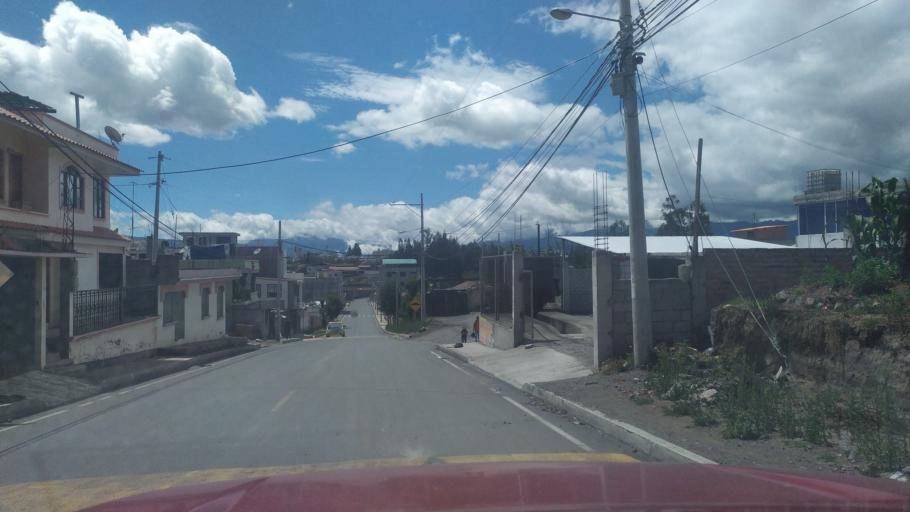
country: EC
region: Chimborazo
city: Riobamba
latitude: -1.6730
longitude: -78.6700
